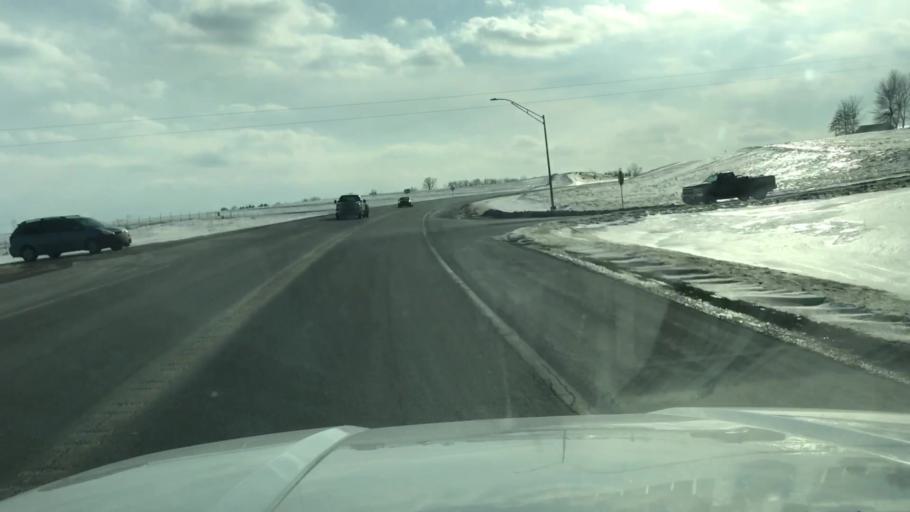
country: US
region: Missouri
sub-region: Nodaway County
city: Maryville
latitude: 40.3347
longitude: -94.8543
